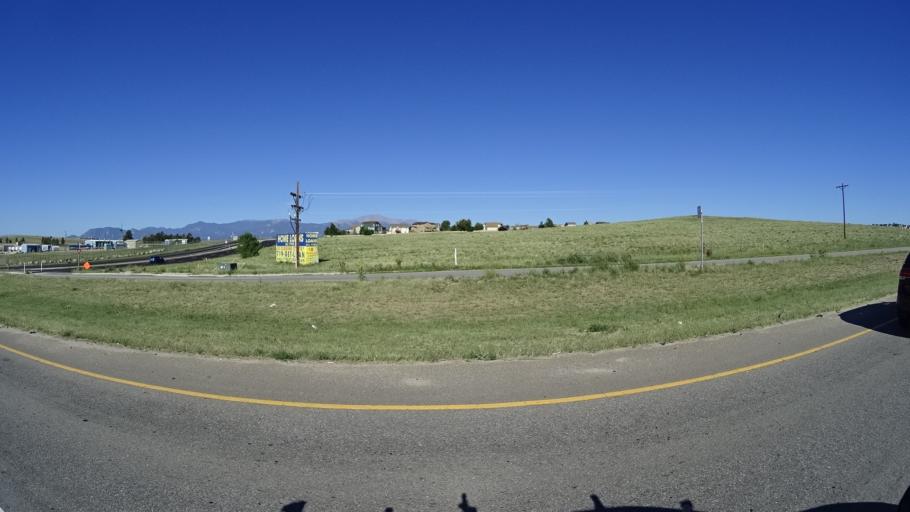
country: US
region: Colorado
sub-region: El Paso County
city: Cimarron Hills
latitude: 38.8878
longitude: -104.6827
